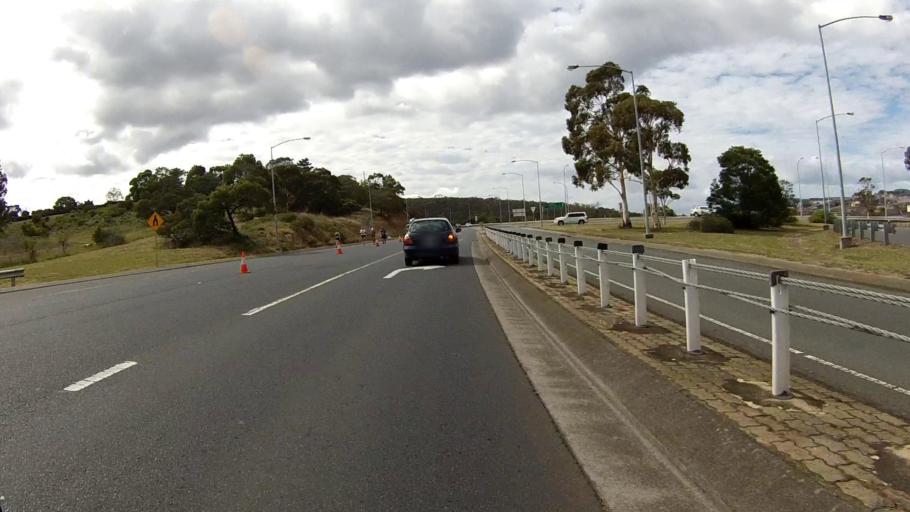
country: AU
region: Tasmania
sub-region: Glenorchy
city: Lutana
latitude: -42.8137
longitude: 147.3145
